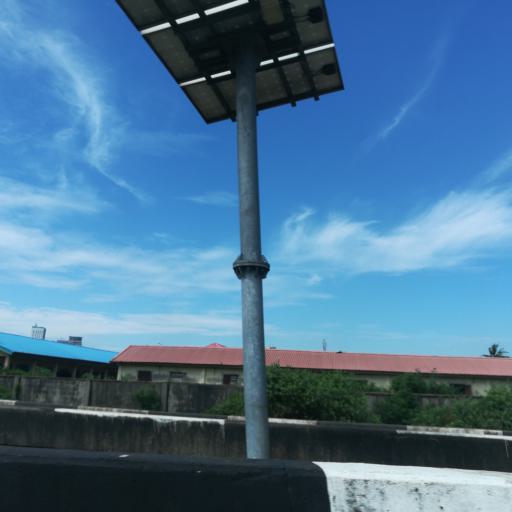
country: NG
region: Lagos
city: Lagos
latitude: 6.4641
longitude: 3.3957
